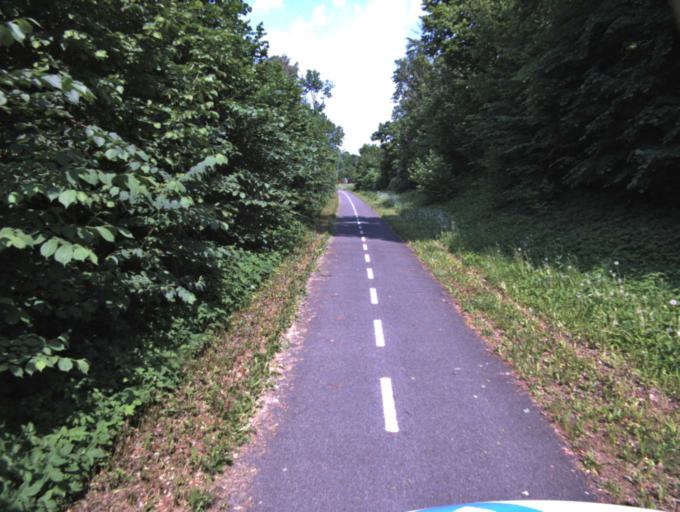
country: SE
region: Skane
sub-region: Kristianstads Kommun
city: Fjalkinge
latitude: 56.0858
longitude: 14.2311
